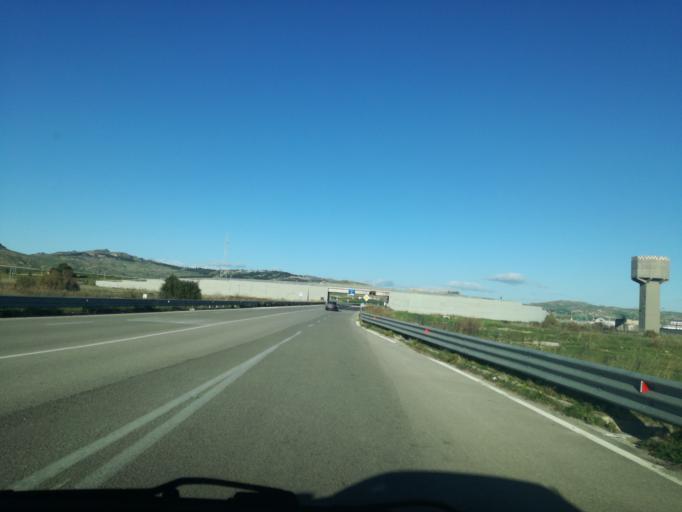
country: IT
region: Sicily
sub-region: Provincia di Caltanissetta
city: Butera
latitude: 37.1272
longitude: 14.1201
